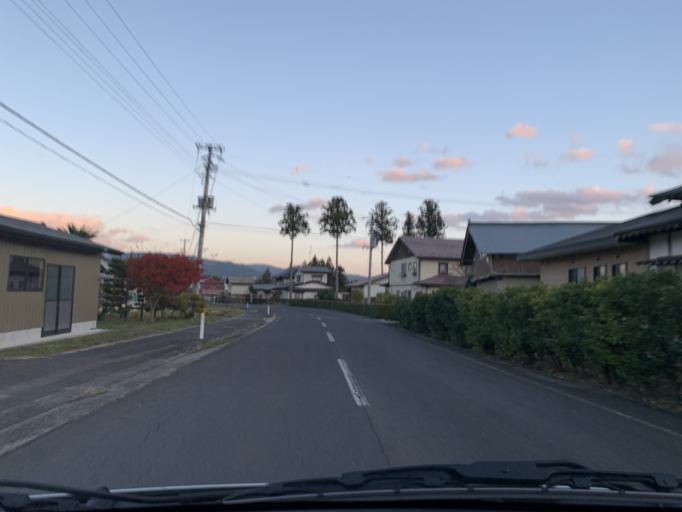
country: JP
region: Iwate
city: Ichinoseki
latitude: 39.0131
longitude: 141.0836
